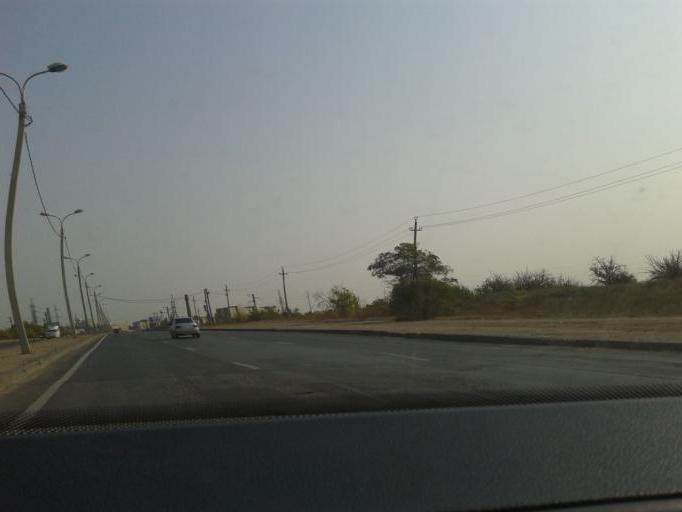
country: RU
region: Volgograd
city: Volgograd
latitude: 48.7402
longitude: 44.4613
